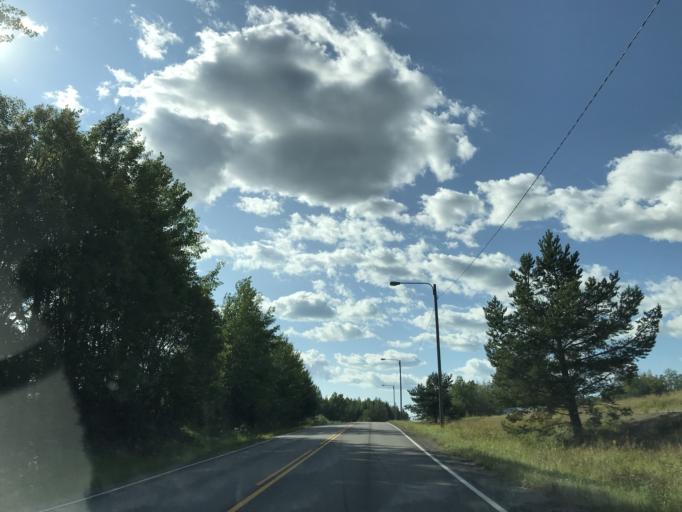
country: FI
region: Uusimaa
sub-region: Helsinki
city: Nurmijaervi
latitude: 60.4335
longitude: 24.8479
